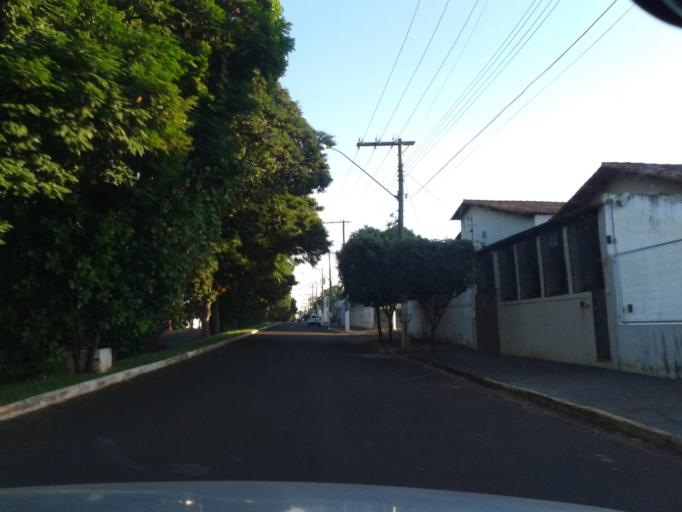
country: BR
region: Minas Gerais
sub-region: Ituiutaba
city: Ituiutaba
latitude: -18.9729
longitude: -49.4670
